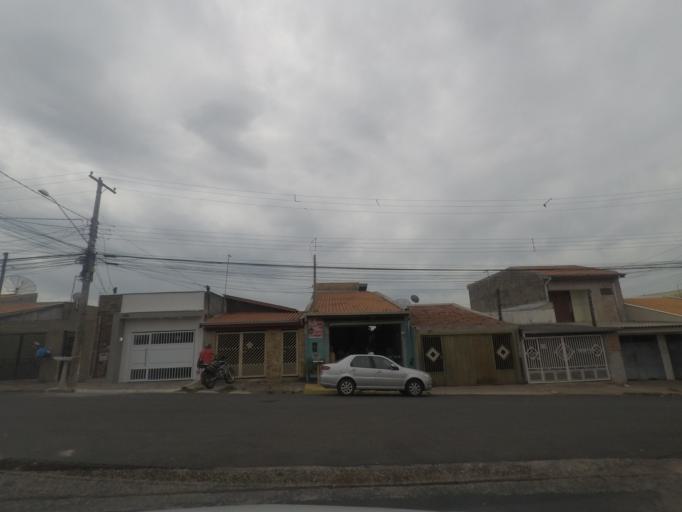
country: BR
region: Sao Paulo
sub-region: Nova Odessa
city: Nova Odessa
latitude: -22.7937
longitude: -47.2818
